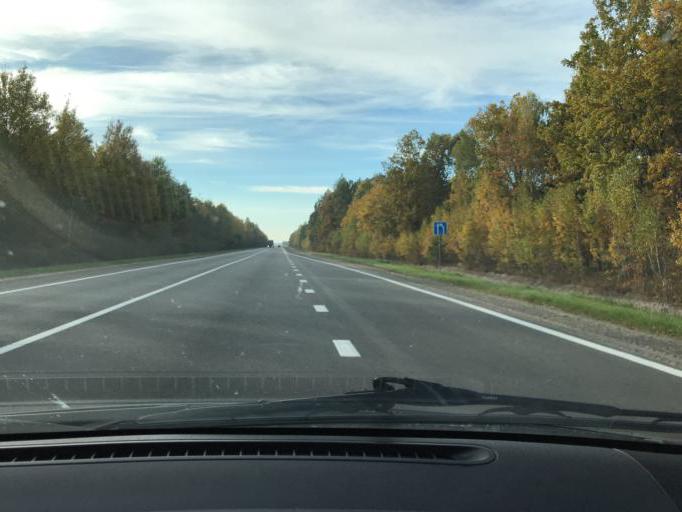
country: BY
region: Brest
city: Ivanava
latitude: 52.1568
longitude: 25.7386
